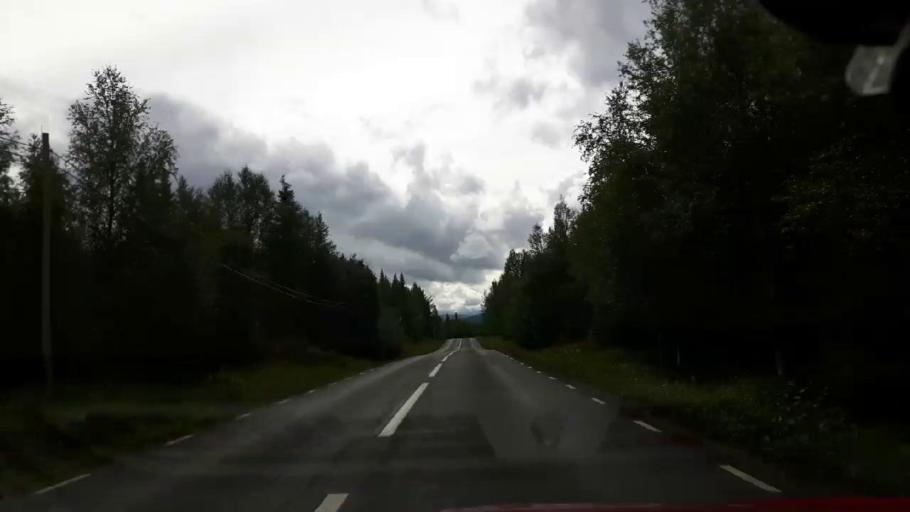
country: NO
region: Nord-Trondelag
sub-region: Lierne
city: Sandvika
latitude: 64.5209
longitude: 14.1633
